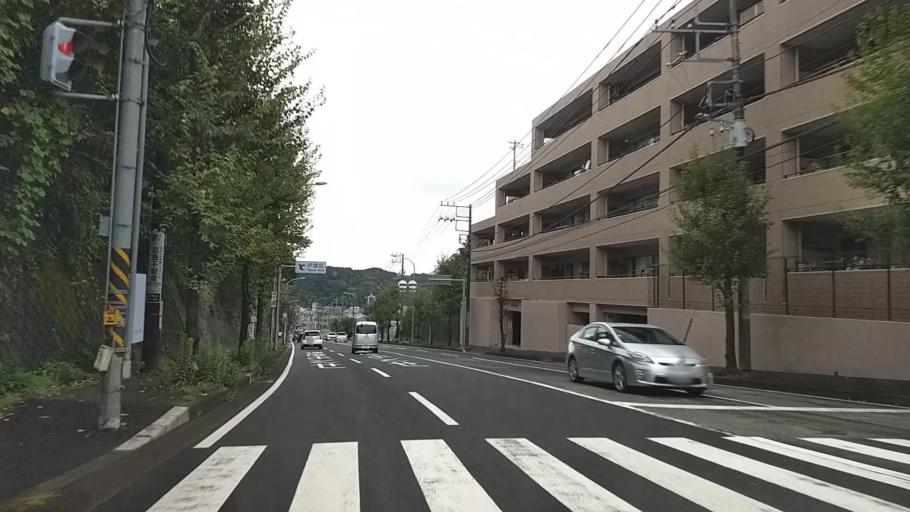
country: JP
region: Kanagawa
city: Kamakura
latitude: 35.4008
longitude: 139.5569
